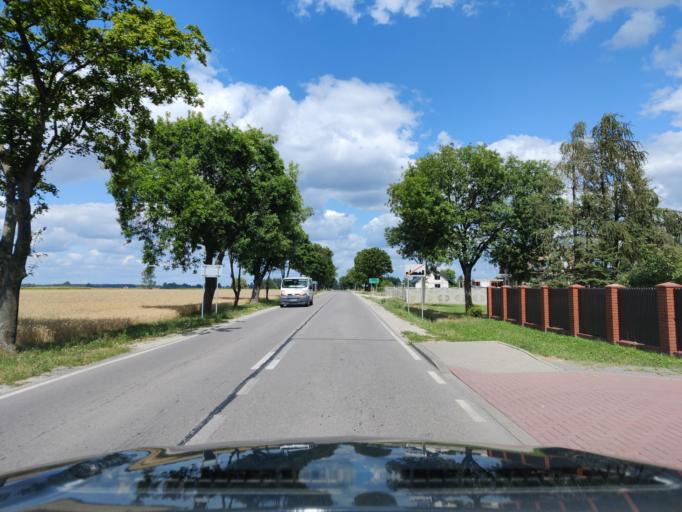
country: PL
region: Masovian Voivodeship
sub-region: Powiat wegrowski
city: Grebkow
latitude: 52.2735
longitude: 21.9163
